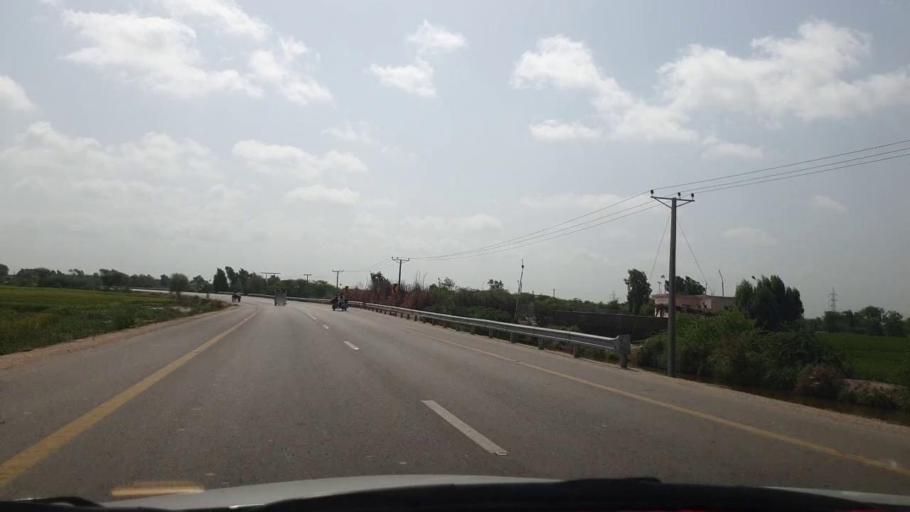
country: PK
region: Sindh
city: Talhar
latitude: 24.9111
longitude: 68.7323
